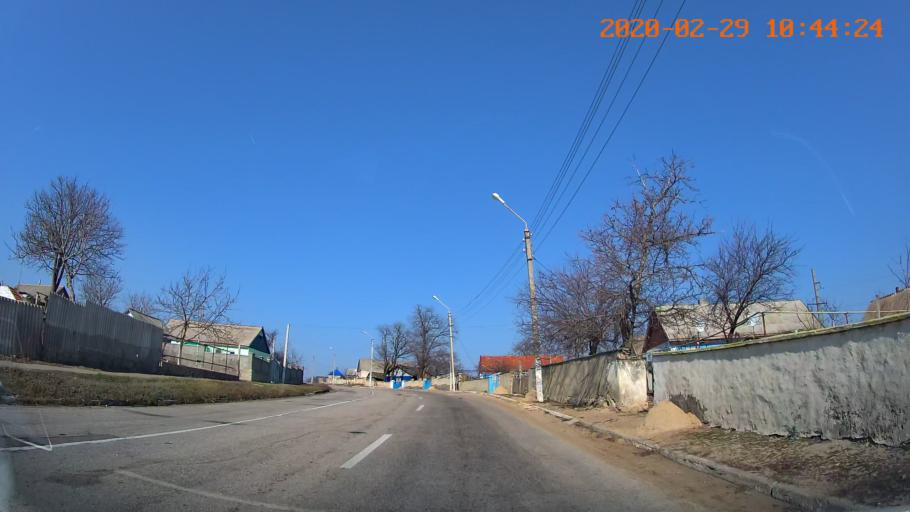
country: MD
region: Telenesti
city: Grigoriopol
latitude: 47.0699
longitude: 29.3954
